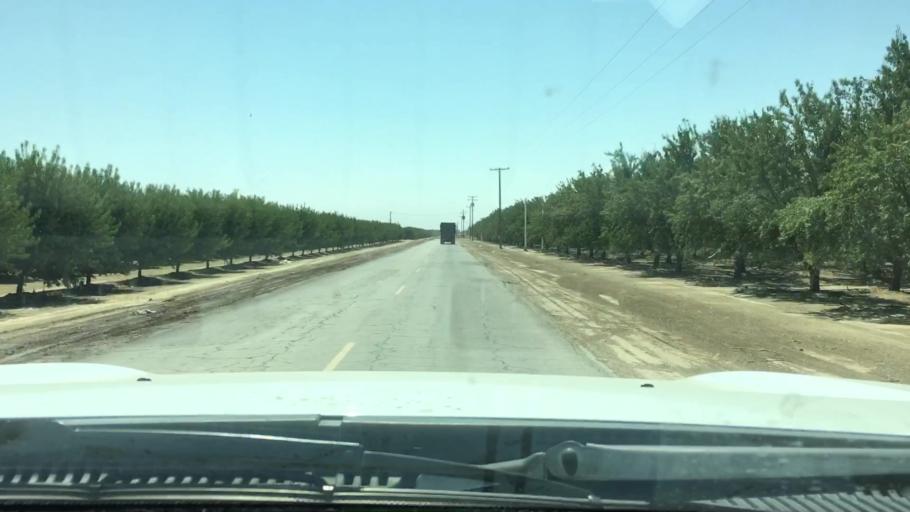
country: US
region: California
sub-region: Kern County
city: Wasco
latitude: 35.5205
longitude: -119.4033
